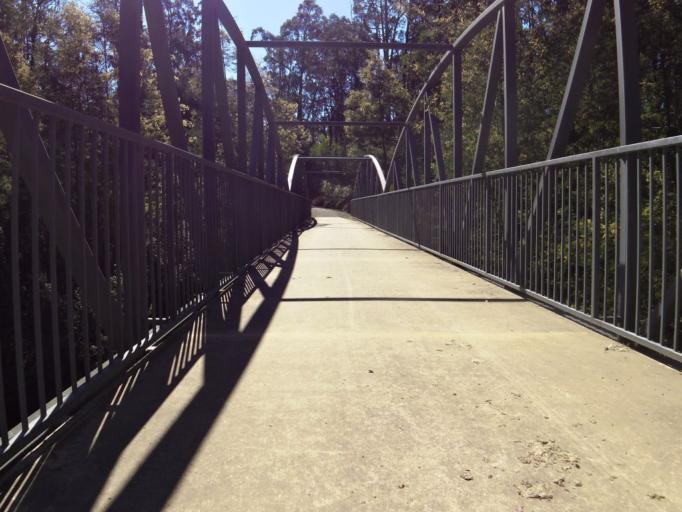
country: AU
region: Victoria
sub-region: Latrobe
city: Moe
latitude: -38.3774
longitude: 146.2403
